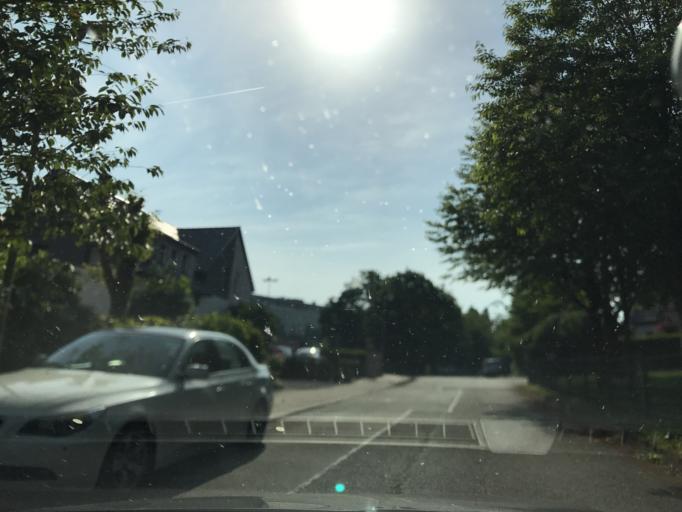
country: DE
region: North Rhine-Westphalia
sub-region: Regierungsbezirk Dusseldorf
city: Essen
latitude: 51.4143
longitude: 6.9759
